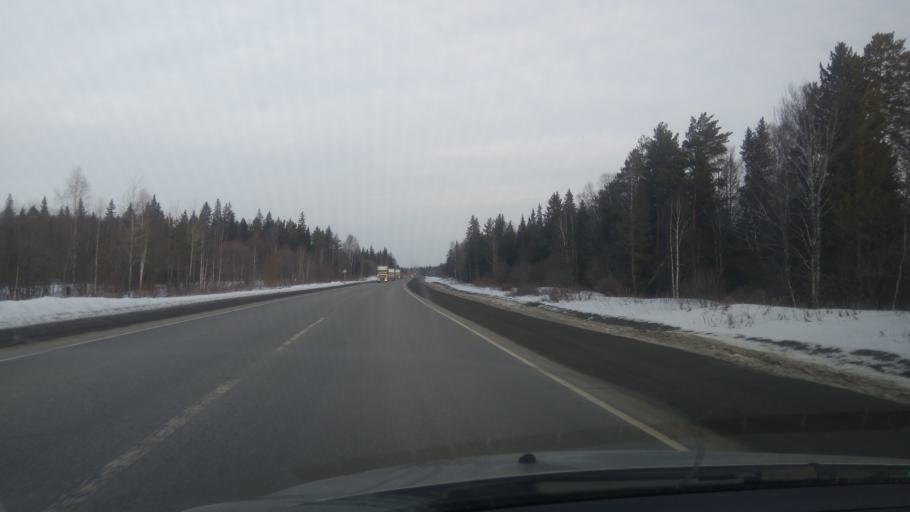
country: RU
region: Sverdlovsk
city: Atig
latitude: 56.8045
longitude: 59.3748
